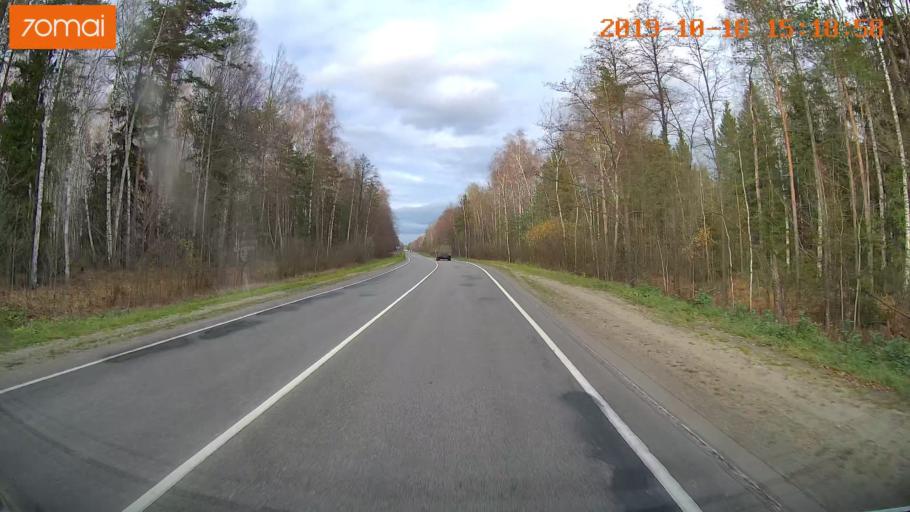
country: RU
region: Vladimir
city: Anopino
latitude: 55.6663
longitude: 40.7341
